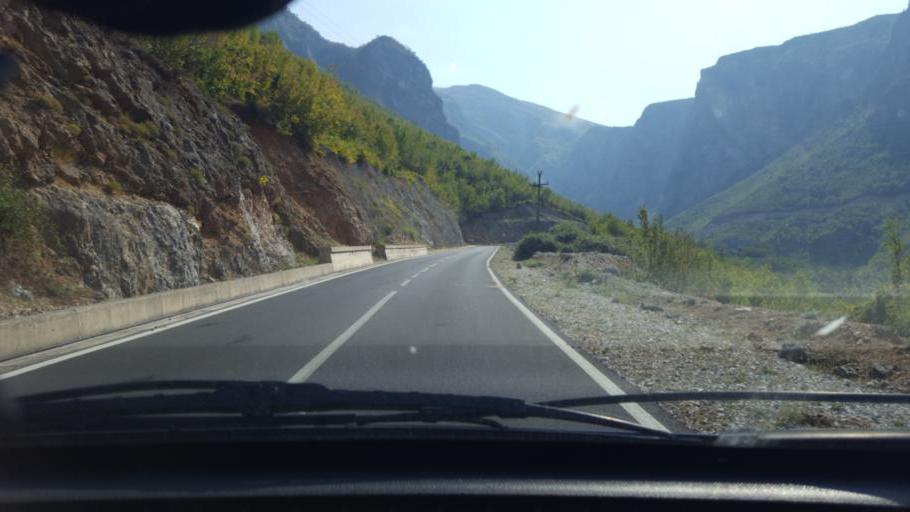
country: AL
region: Shkoder
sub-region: Rrethi i Malesia e Madhe
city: Kastrat
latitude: 42.4222
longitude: 19.5105
